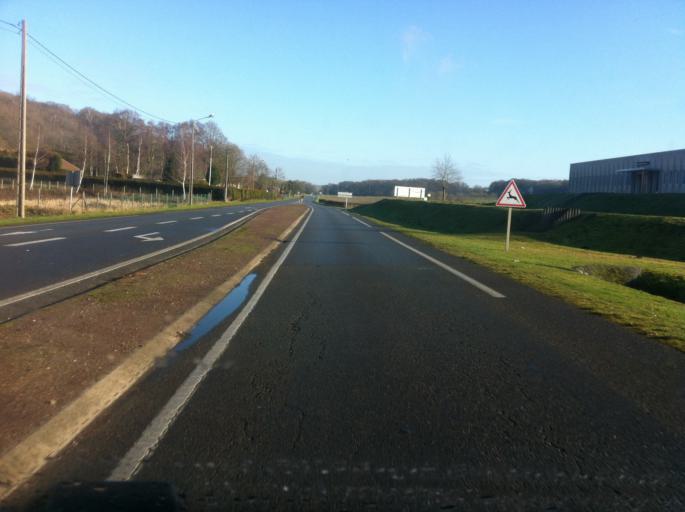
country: FR
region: Haute-Normandie
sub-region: Departement de la Seine-Maritime
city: Yainville
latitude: 49.4604
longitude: 0.8369
